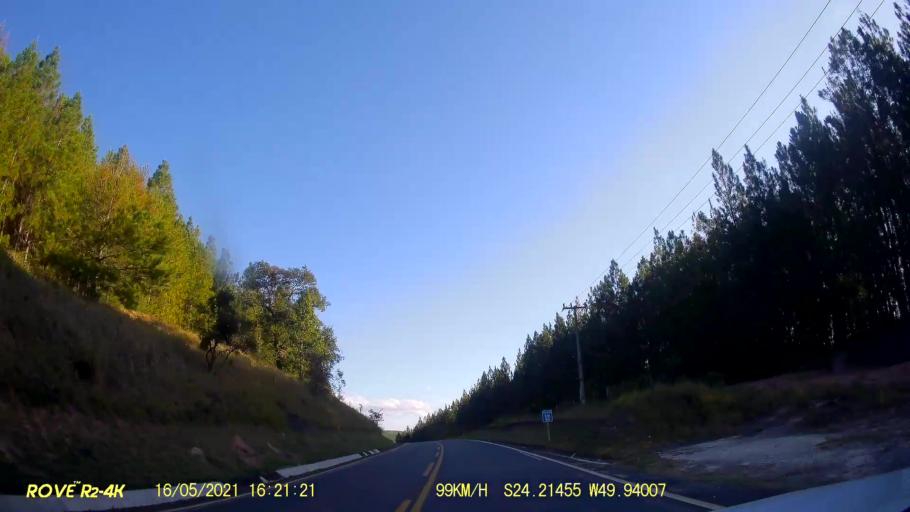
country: BR
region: Parana
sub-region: Jaguariaiva
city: Jaguariaiva
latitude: -24.2147
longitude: -49.9403
